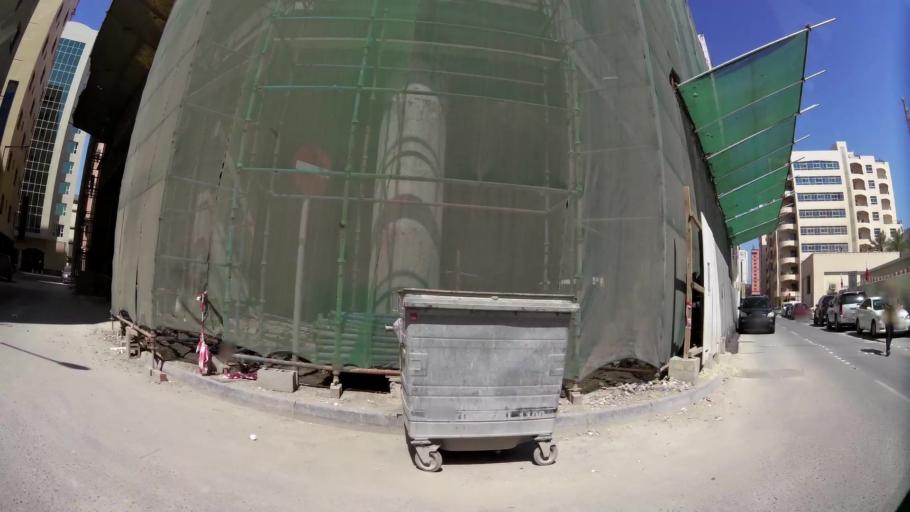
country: BH
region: Manama
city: Manama
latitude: 26.2129
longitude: 50.6077
